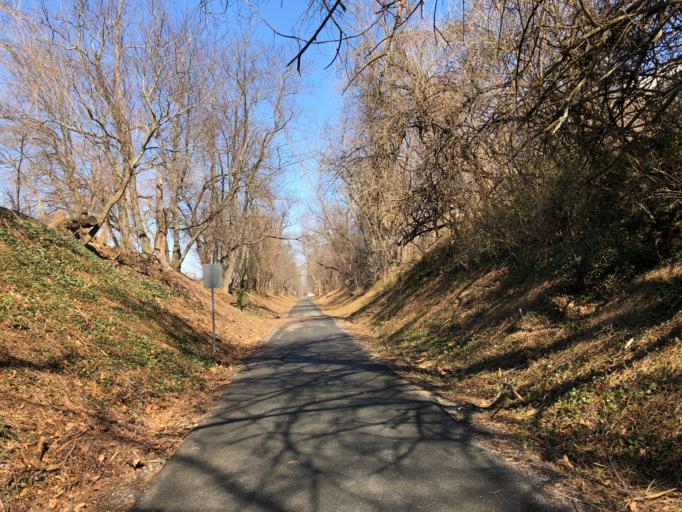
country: US
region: Maryland
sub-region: Kent County
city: Chestertown
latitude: 39.2191
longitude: -76.0719
